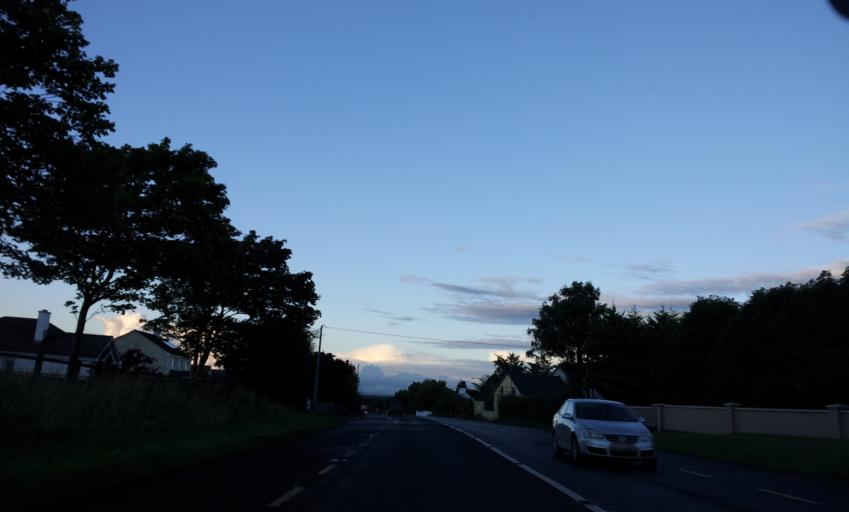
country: IE
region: Munster
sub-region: County Limerick
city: Newcastle West
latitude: 52.4573
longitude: -9.0344
